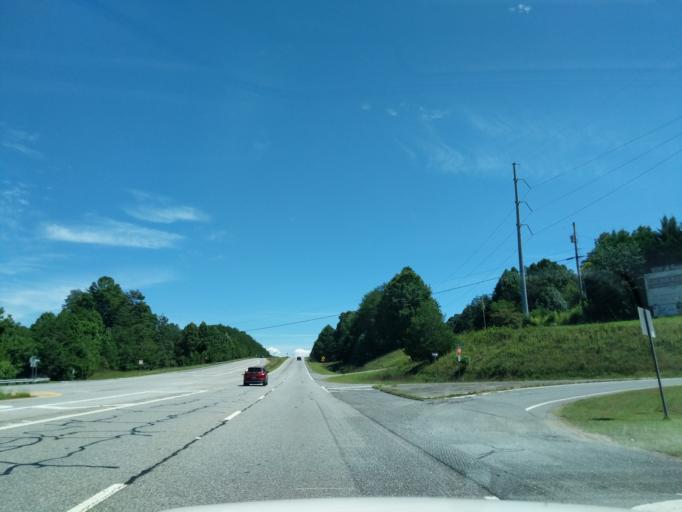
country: US
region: Georgia
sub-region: Fannin County
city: Blue Ridge
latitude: 34.8928
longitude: -84.2487
